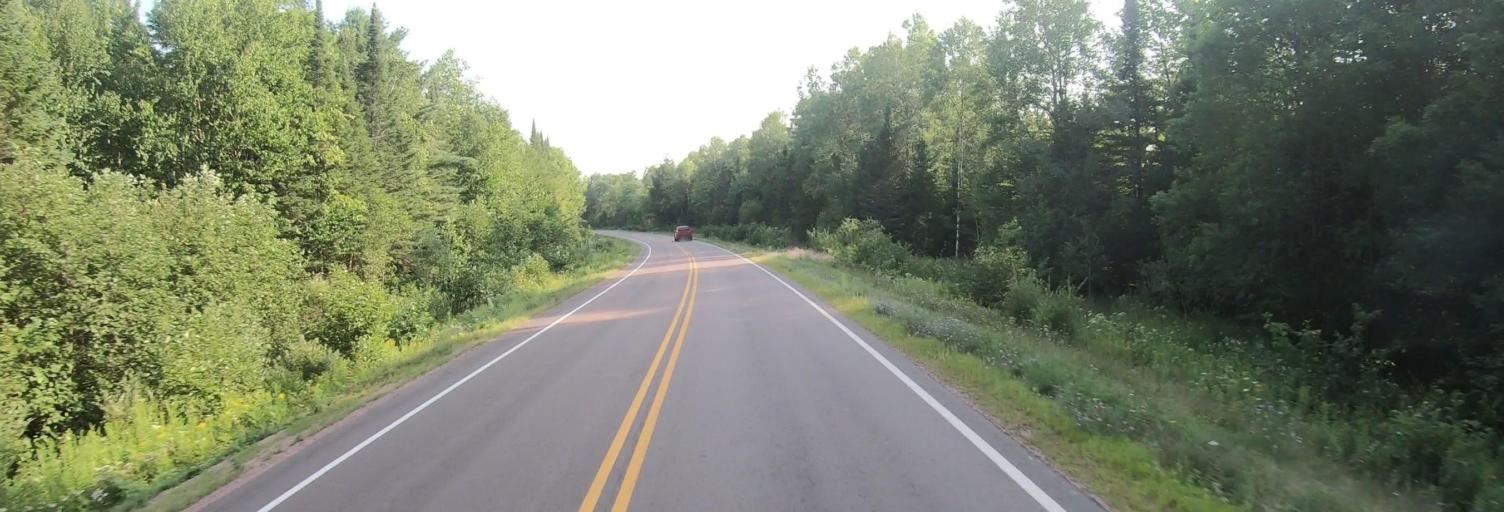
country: US
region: Wisconsin
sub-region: Ashland County
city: Ashland
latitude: 46.2420
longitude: -90.8347
